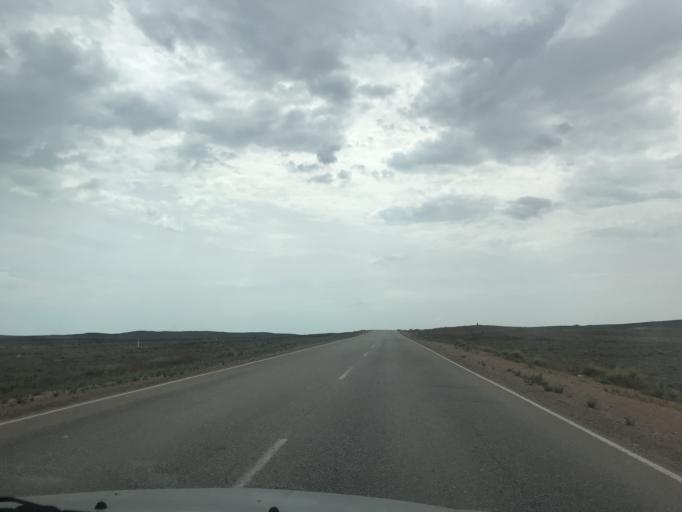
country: KZ
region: Zhambyl
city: Mynaral
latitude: 45.4919
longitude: 73.5276
